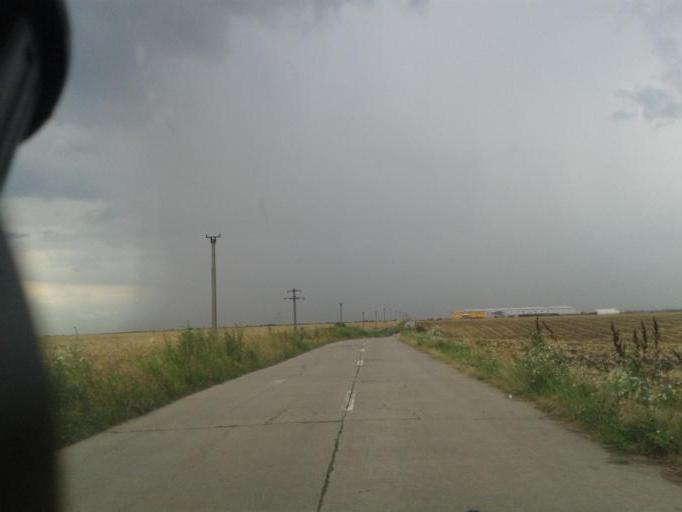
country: RO
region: Ialomita
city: Sinesti
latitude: 44.5426
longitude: 26.4096
